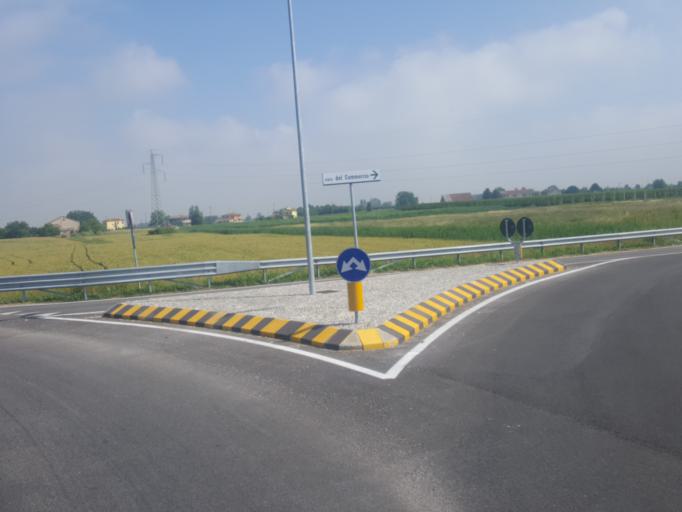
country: IT
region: Veneto
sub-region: Provincia di Rovigo
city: Stienta
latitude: 44.9347
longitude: 11.5564
